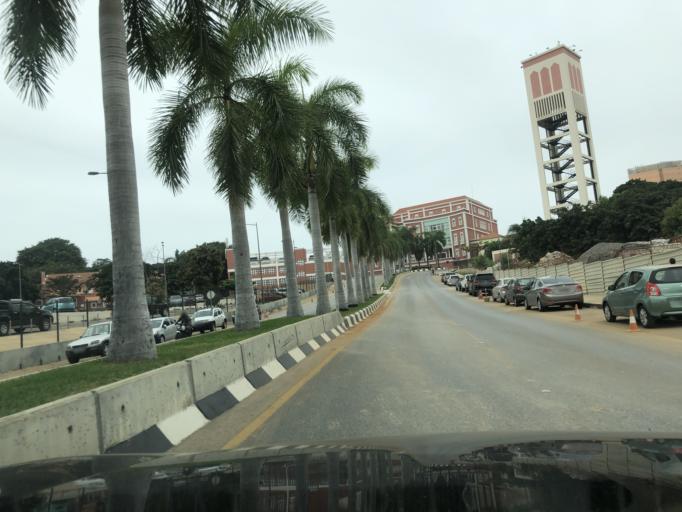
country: AO
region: Luanda
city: Luanda
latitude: -8.8202
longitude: 13.2243
